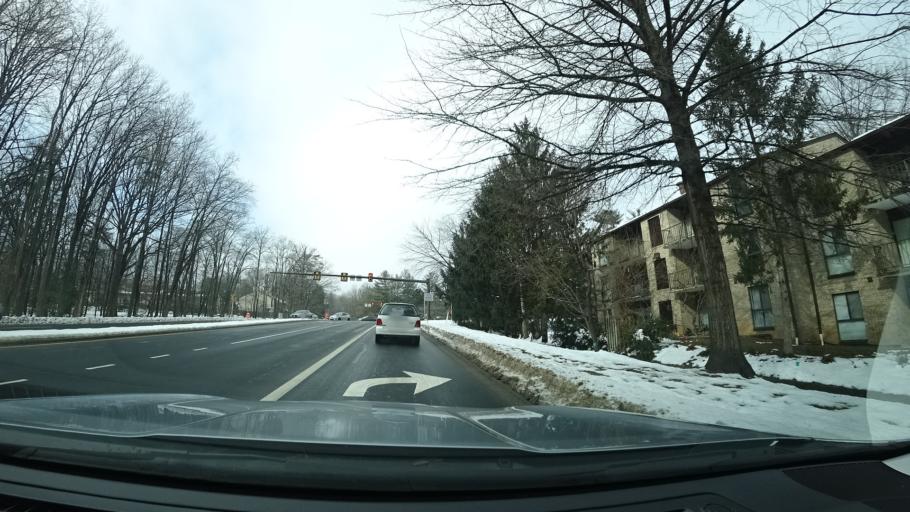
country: US
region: Virginia
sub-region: Fairfax County
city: Reston
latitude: 38.9427
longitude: -77.3603
